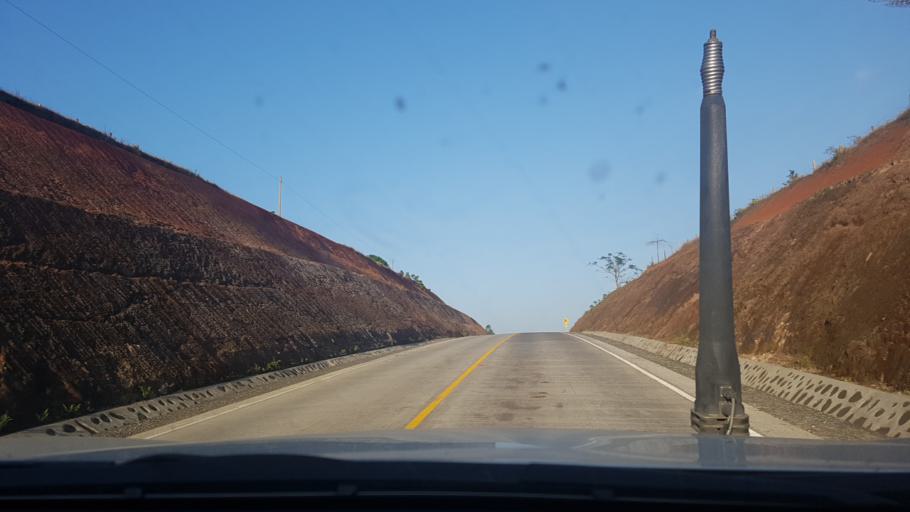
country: NI
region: Atlantico Sur
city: Rama
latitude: 11.8183
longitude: -84.0954
